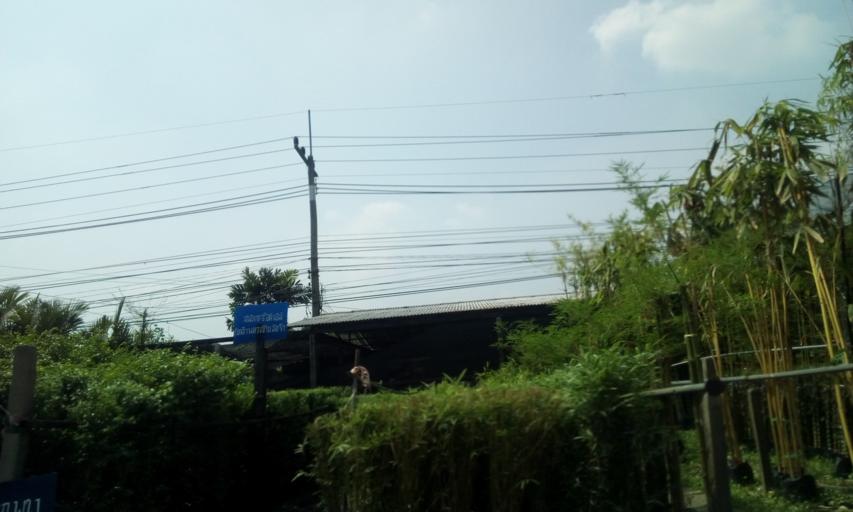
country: TH
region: Nakhon Nayok
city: Ongkharak
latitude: 14.1100
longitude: 100.9435
